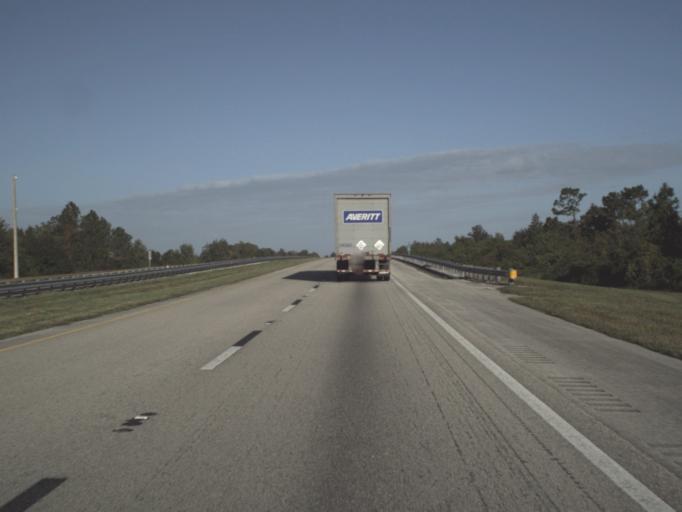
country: US
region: Florida
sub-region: Indian River County
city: Fellsmere
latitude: 27.7192
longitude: -80.9034
